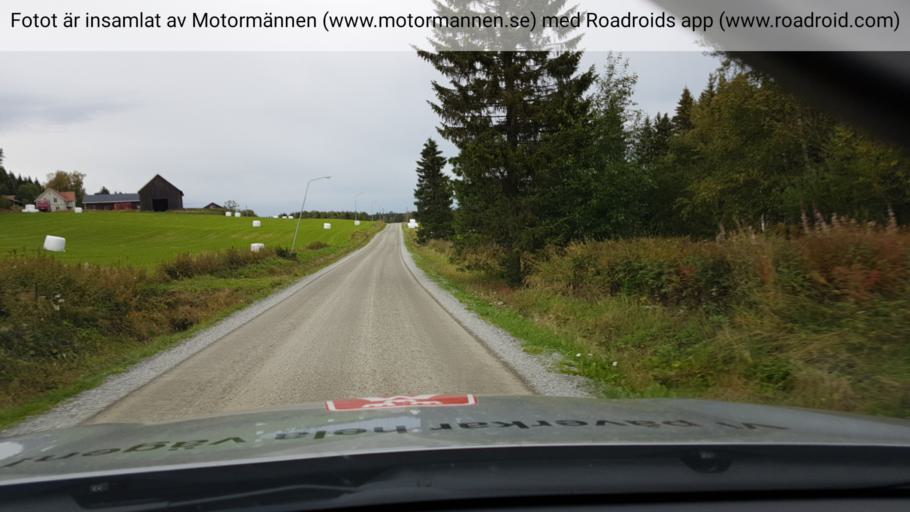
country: SE
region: Jaemtland
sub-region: Bergs Kommun
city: Hoverberg
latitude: 62.9472
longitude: 14.2682
